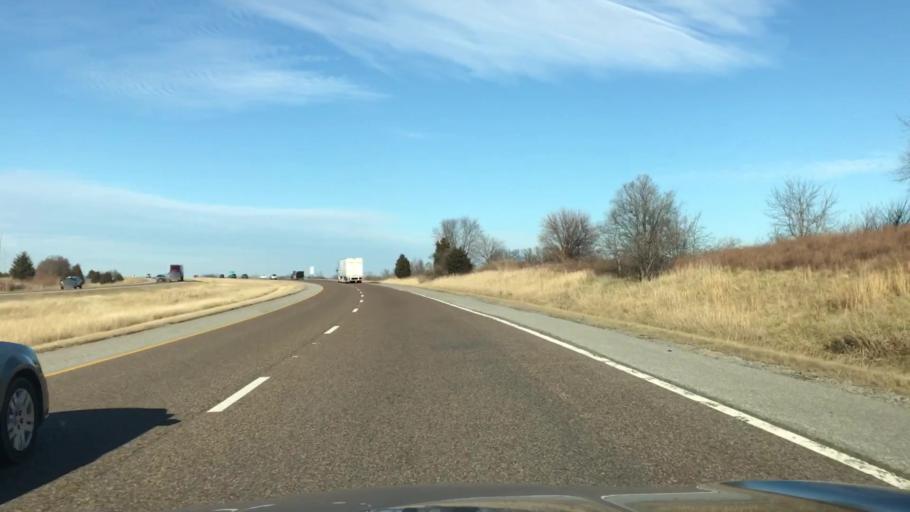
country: US
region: Illinois
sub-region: Macoupin County
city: Staunton
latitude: 38.9719
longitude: -89.7497
